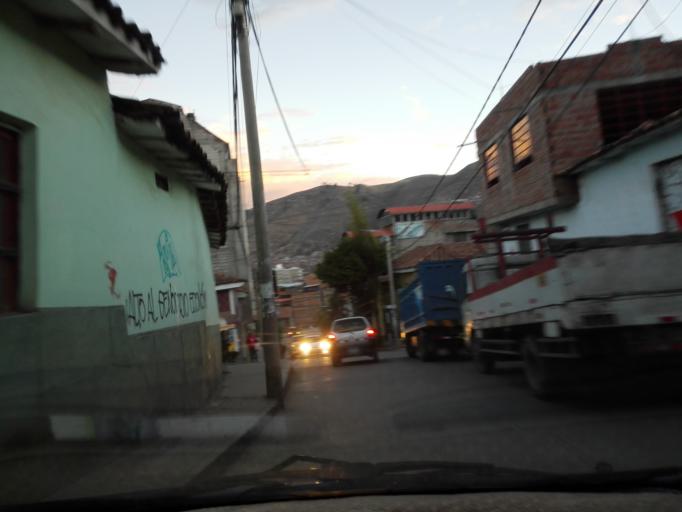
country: PE
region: Cusco
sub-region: Provincia de Cusco
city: Cusco
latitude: -13.5263
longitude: -71.9636
